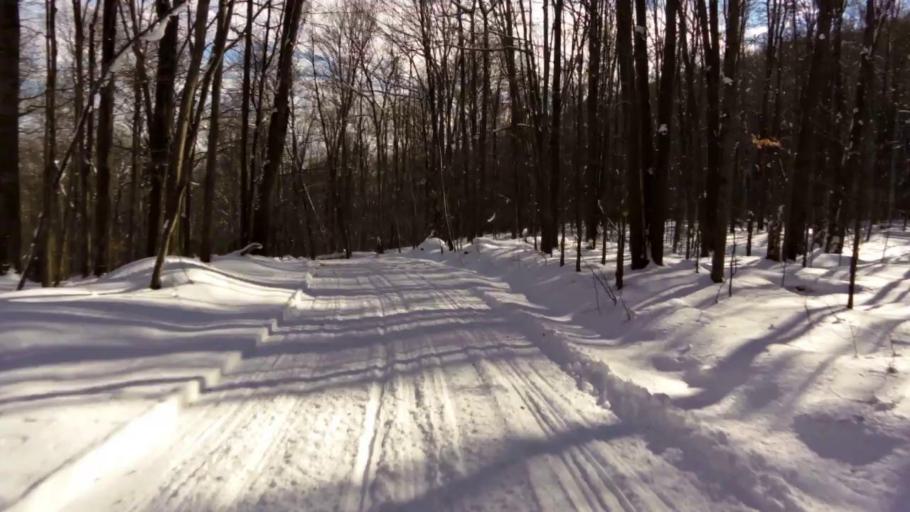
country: US
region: Pennsylvania
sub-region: McKean County
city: Foster Brook
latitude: 42.0660
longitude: -78.6618
